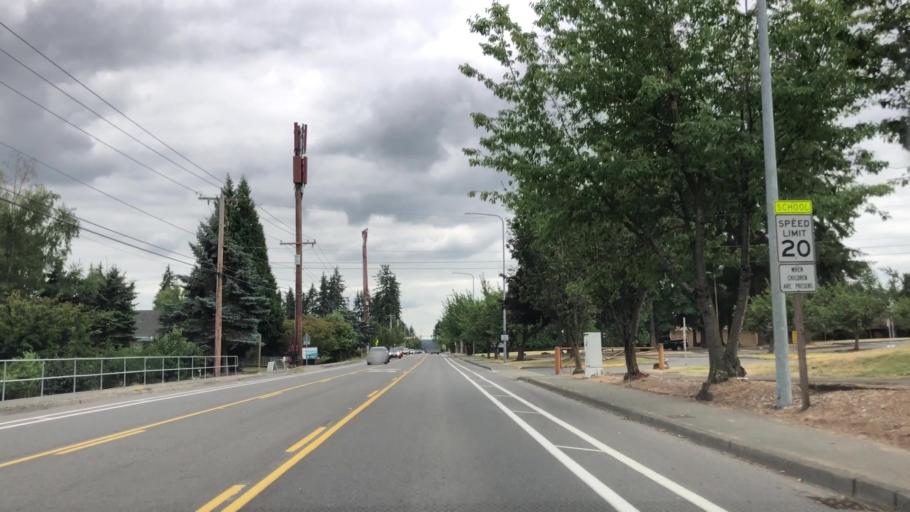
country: US
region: Washington
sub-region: King County
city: Kingsgate
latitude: 47.7289
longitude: -122.1640
